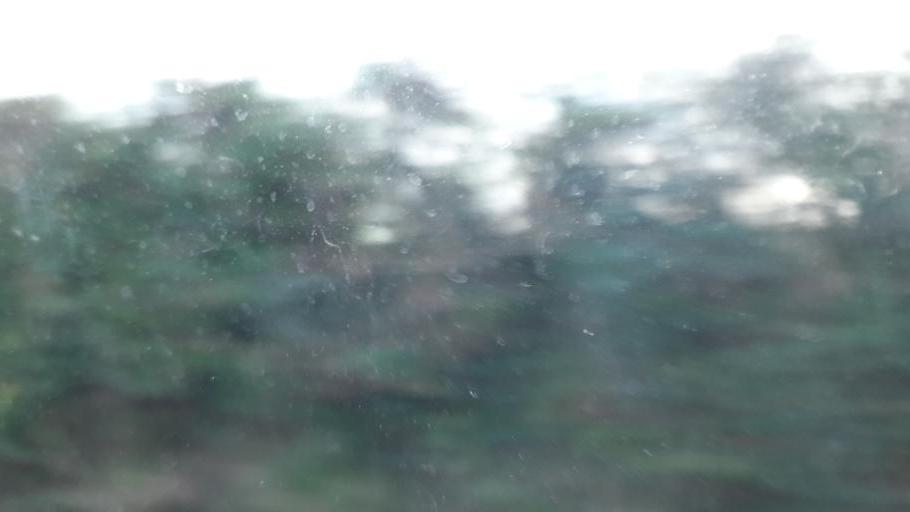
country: IE
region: Leinster
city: Balrothery
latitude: 53.5742
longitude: -6.1492
